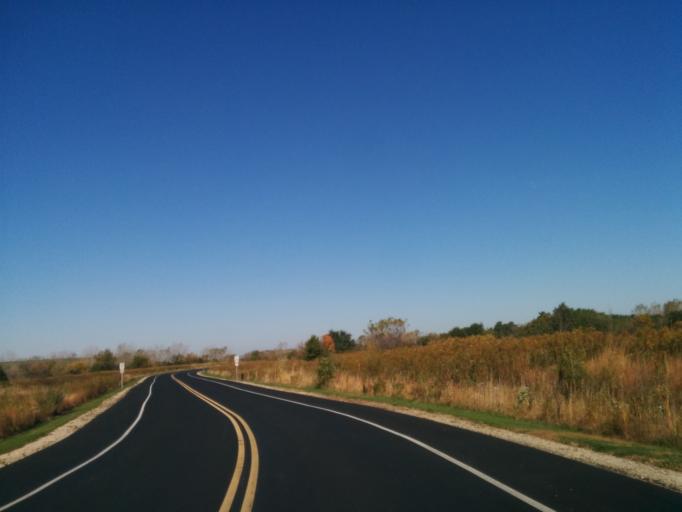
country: US
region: Illinois
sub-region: DuPage County
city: Carol Stream
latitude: 41.9559
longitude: -88.1261
